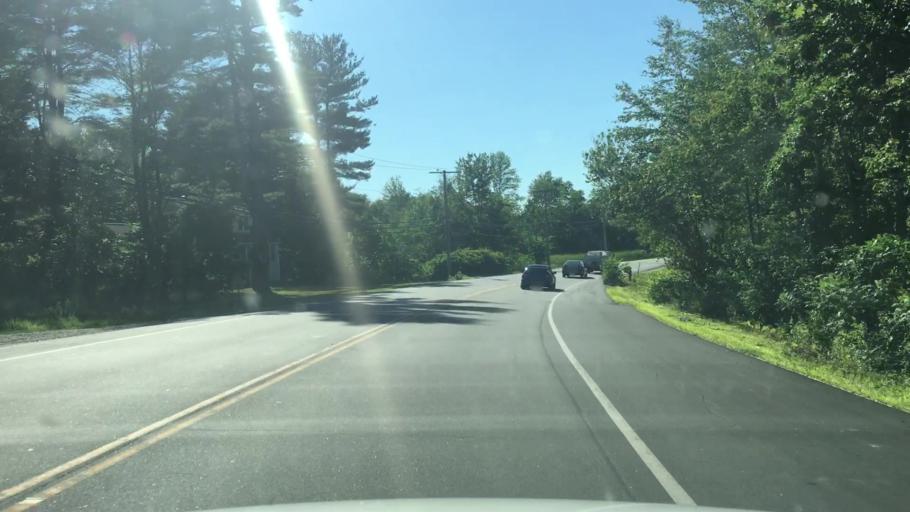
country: US
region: New Hampshire
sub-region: Rockingham County
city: Exeter
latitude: 43.0084
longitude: -70.9972
